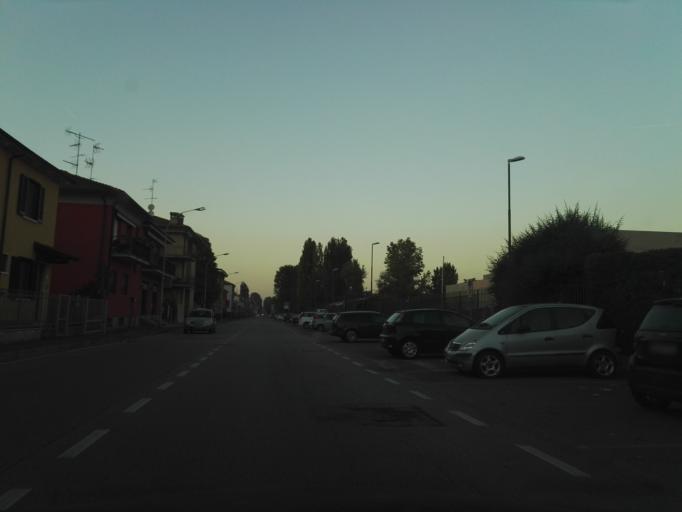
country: IT
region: Lombardy
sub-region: Citta metropolitana di Milano
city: Mezzate
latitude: 45.4374
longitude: 9.2954
